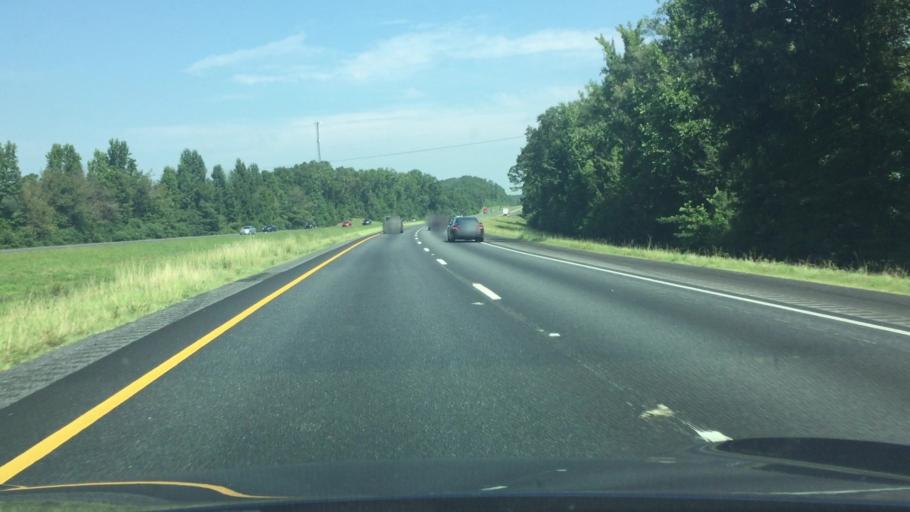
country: US
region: Alabama
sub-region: Chilton County
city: Jemison
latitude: 33.0111
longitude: -86.7102
